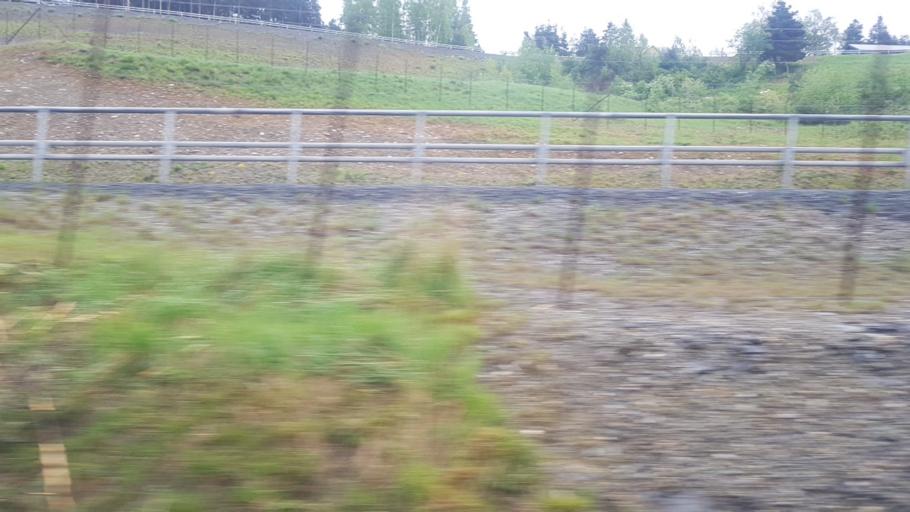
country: NO
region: Oppland
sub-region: Sor-Fron
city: Hundorp
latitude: 61.5611
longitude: 9.9247
